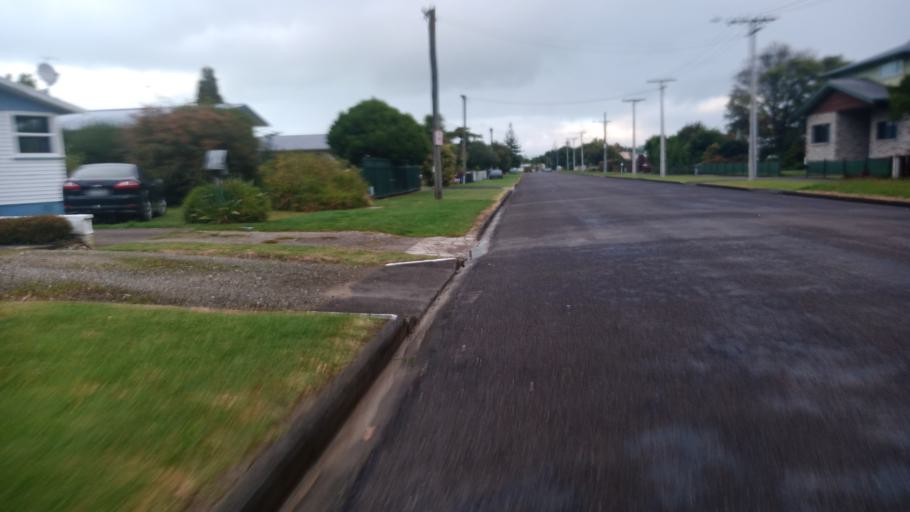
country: NZ
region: Gisborne
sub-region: Gisborne District
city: Gisborne
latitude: -38.6410
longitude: 178.0132
